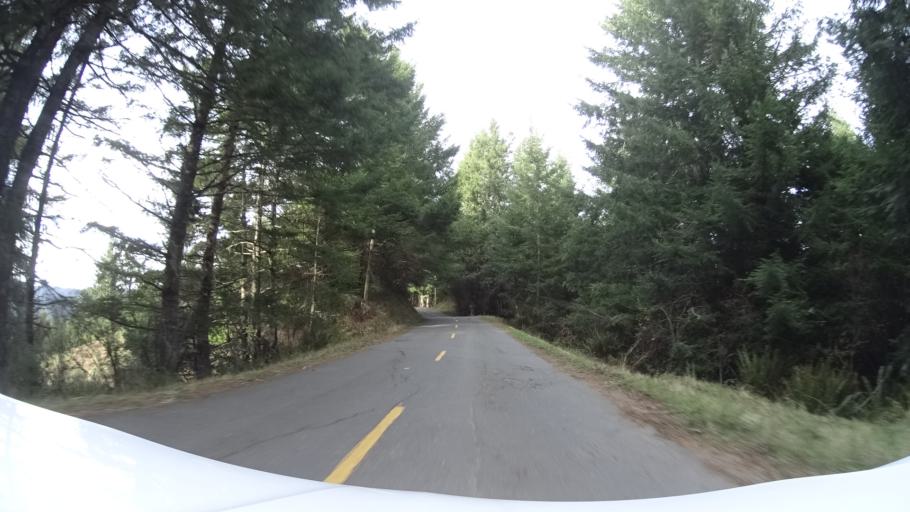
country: US
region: California
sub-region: Humboldt County
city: Ferndale
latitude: 40.5242
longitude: -124.2666
